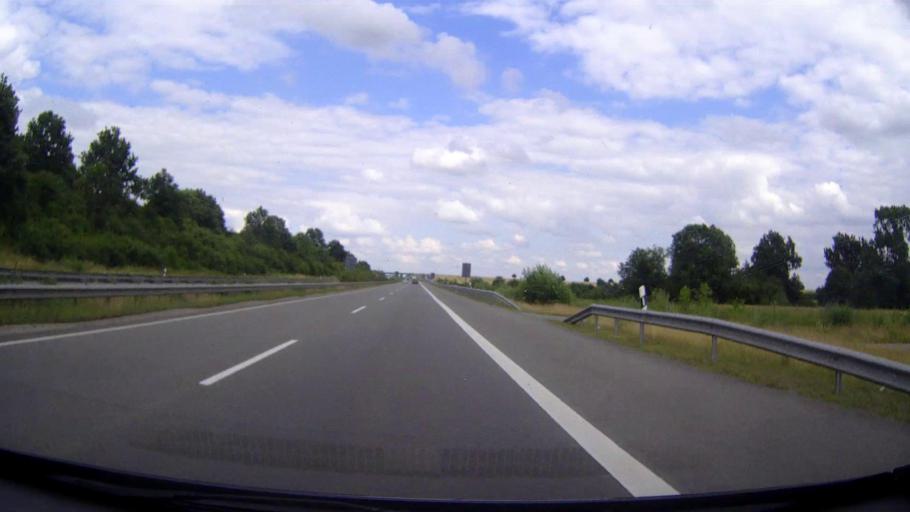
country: DE
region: Schleswig-Holstein
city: Weede
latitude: 53.9185
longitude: 10.3683
